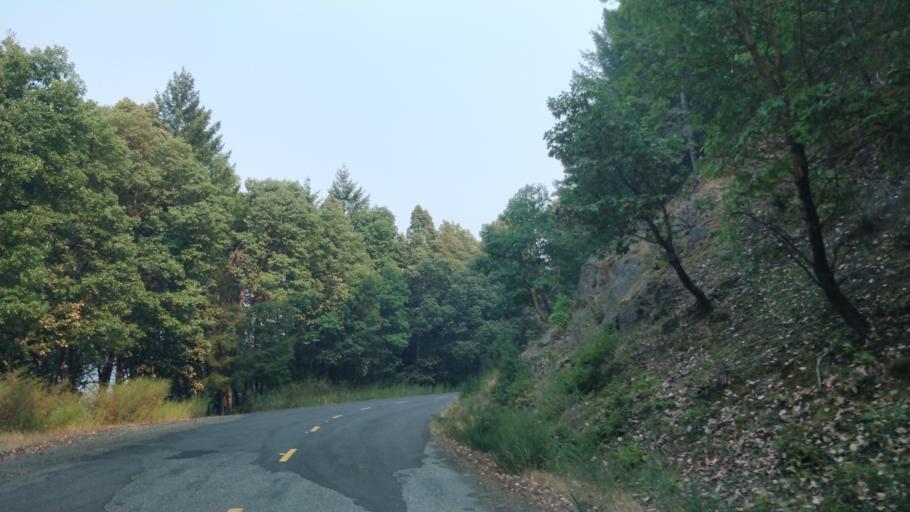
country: US
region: California
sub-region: Humboldt County
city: Rio Dell
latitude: 40.2631
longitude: -124.1071
